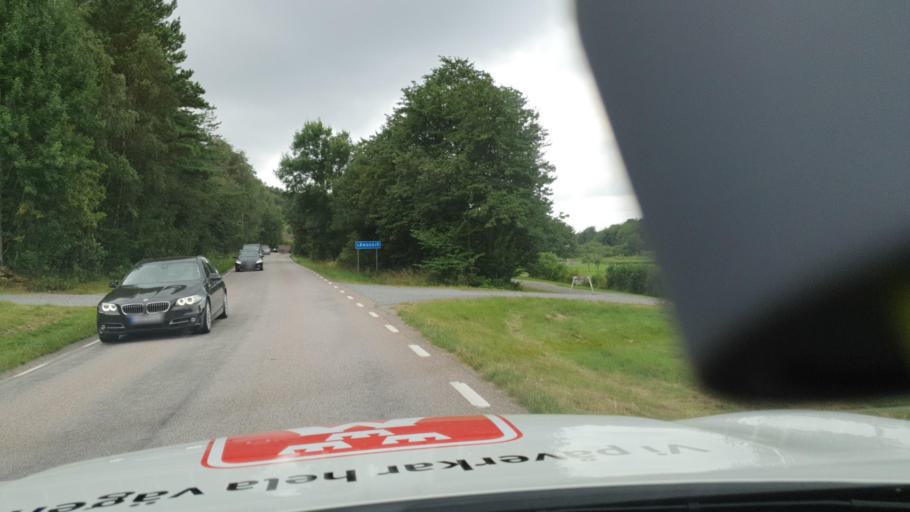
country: SE
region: Vaestra Goetaland
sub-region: Tanums Kommun
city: Grebbestad
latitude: 58.6358
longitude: 11.2896
